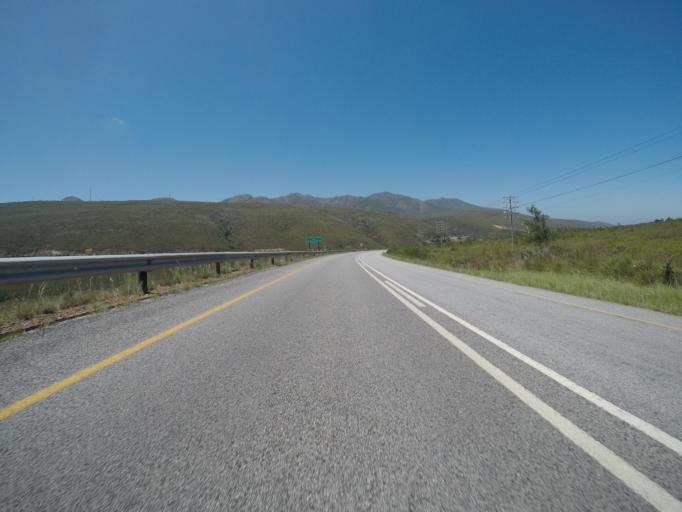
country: ZA
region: Eastern Cape
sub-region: Cacadu District Municipality
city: Kareedouw
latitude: -33.9431
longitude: 24.3069
